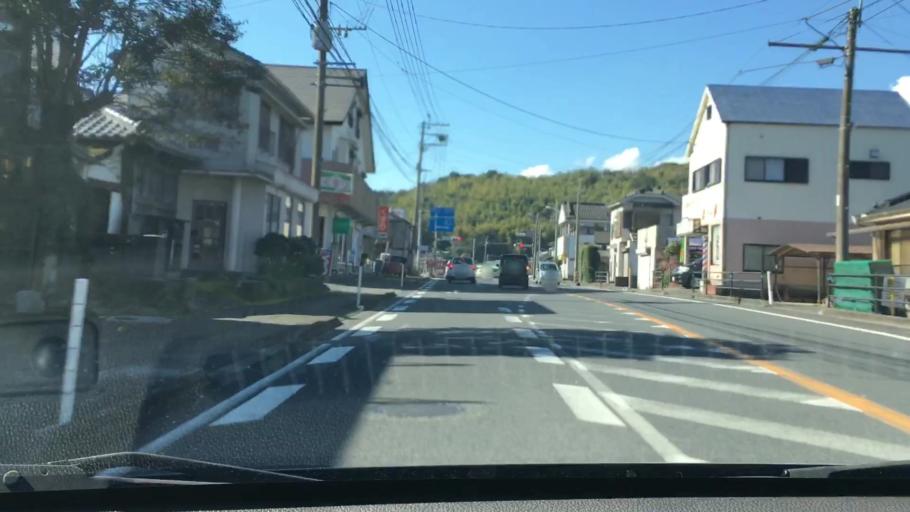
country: JP
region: Kagoshima
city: Ijuin
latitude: 31.6625
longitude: 130.4876
